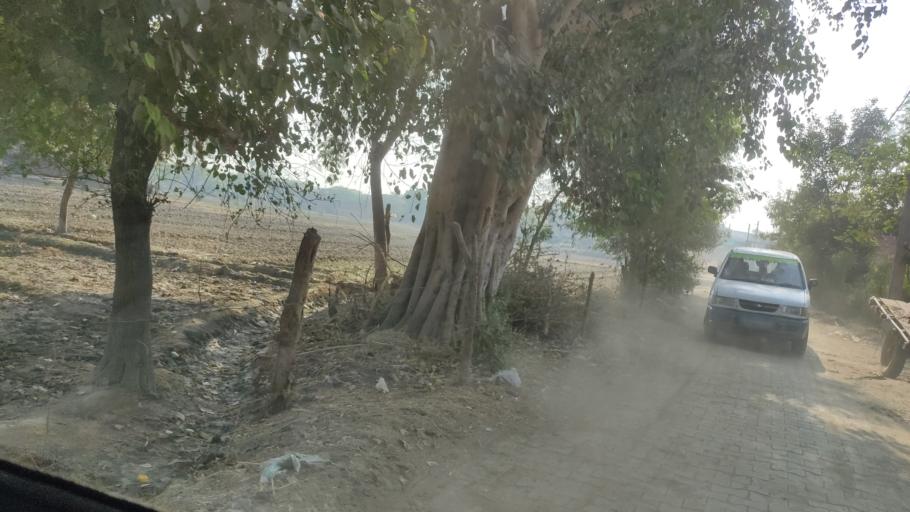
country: IN
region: Uttar Pradesh
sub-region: Mathura
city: Radha Kund
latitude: 27.5611
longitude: 77.5579
